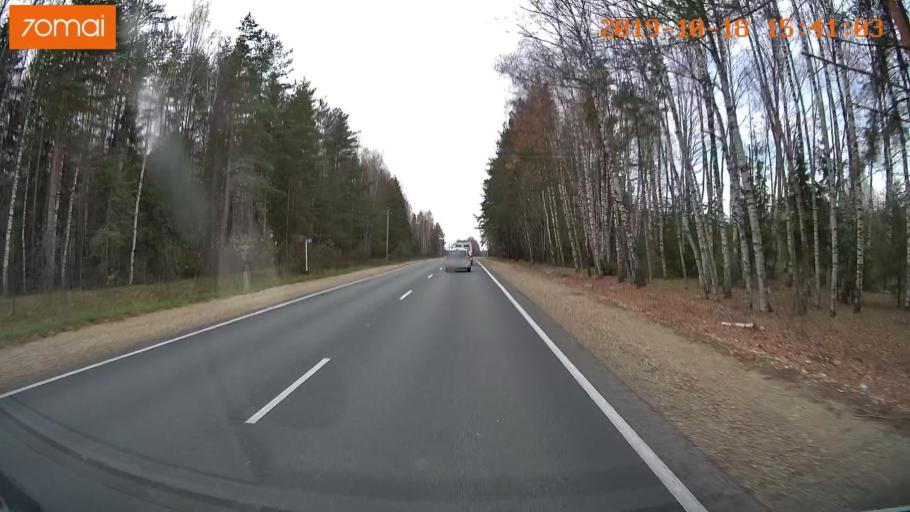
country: RU
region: Vladimir
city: Golovino
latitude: 55.9414
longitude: 40.5879
